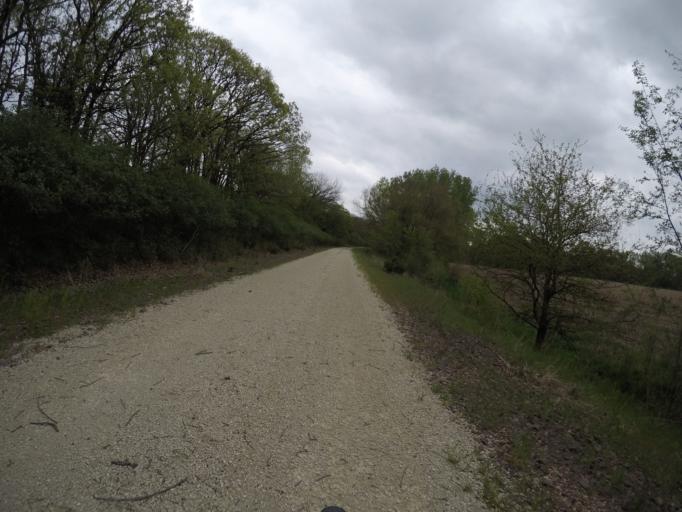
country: US
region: Nebraska
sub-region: Gage County
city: Wymore
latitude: 40.1246
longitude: -96.6414
